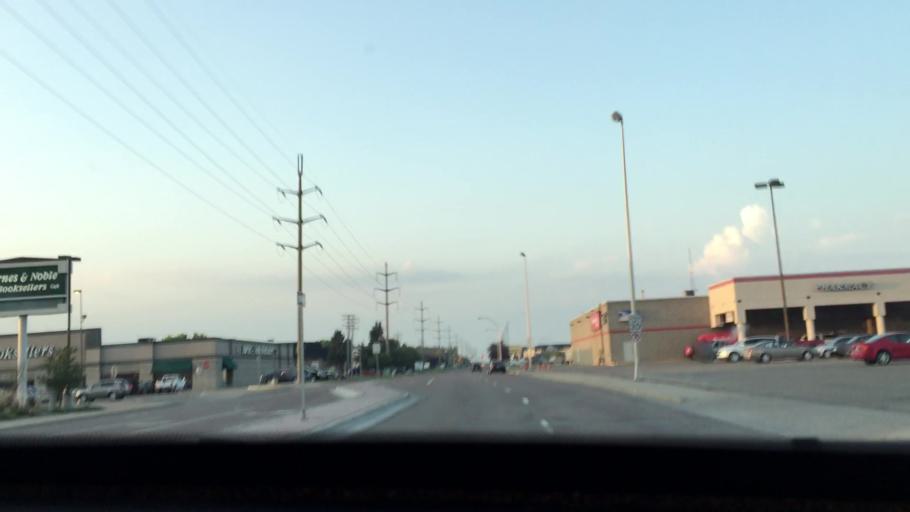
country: US
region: North Dakota
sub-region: Cass County
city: West Fargo
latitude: 46.8622
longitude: -96.8508
